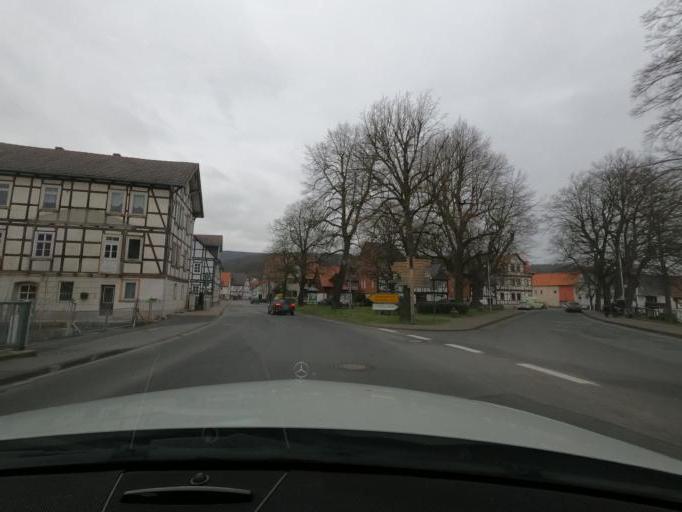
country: DE
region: Hesse
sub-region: Regierungsbezirk Kassel
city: Eschwege
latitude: 51.2031
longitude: 10.0640
